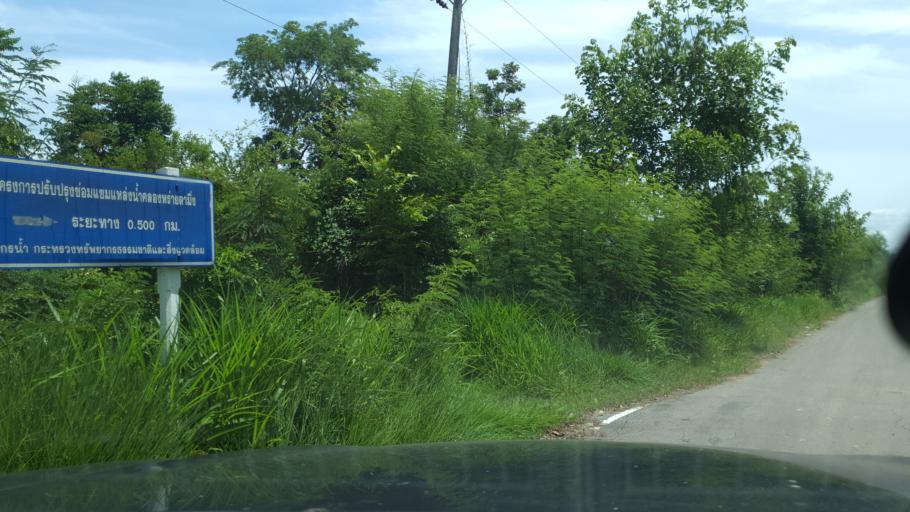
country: TH
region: Sukhothai
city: Ban Na
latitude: 17.0937
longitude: 99.6795
